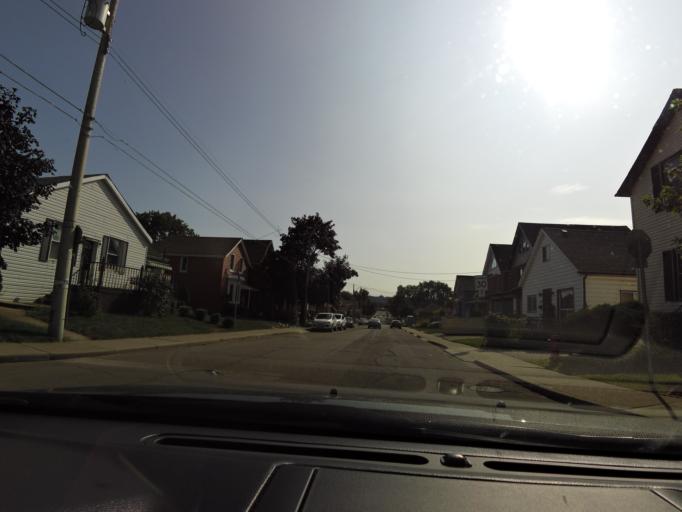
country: CA
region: Ontario
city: Hamilton
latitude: 43.2686
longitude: -79.8582
